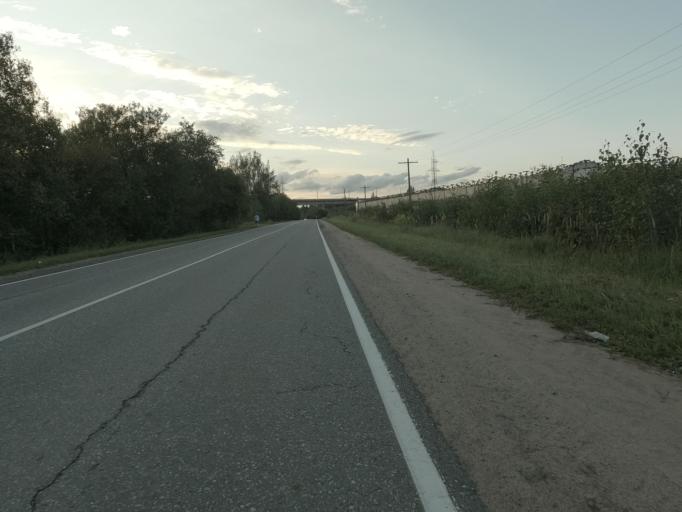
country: RU
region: Leningrad
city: Mga
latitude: 59.7563
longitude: 31.0215
